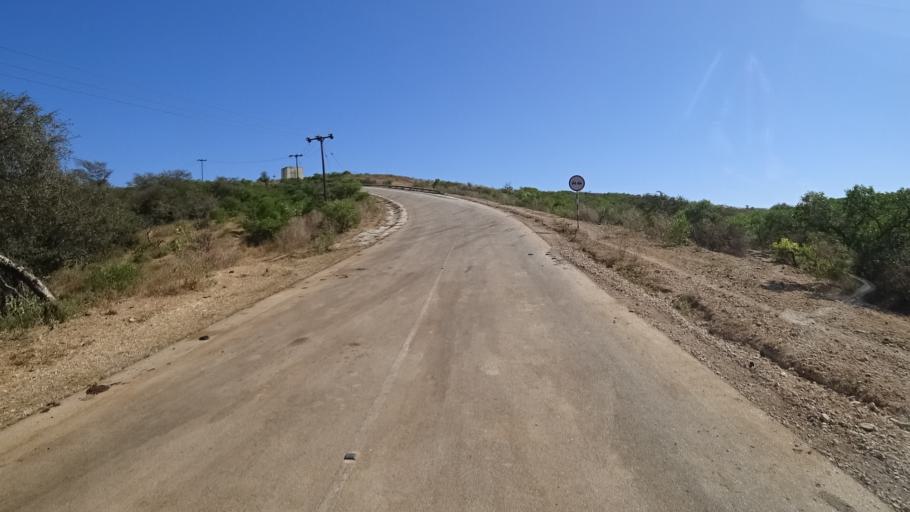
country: YE
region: Al Mahrah
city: Hawf
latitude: 16.7475
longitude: 53.3440
